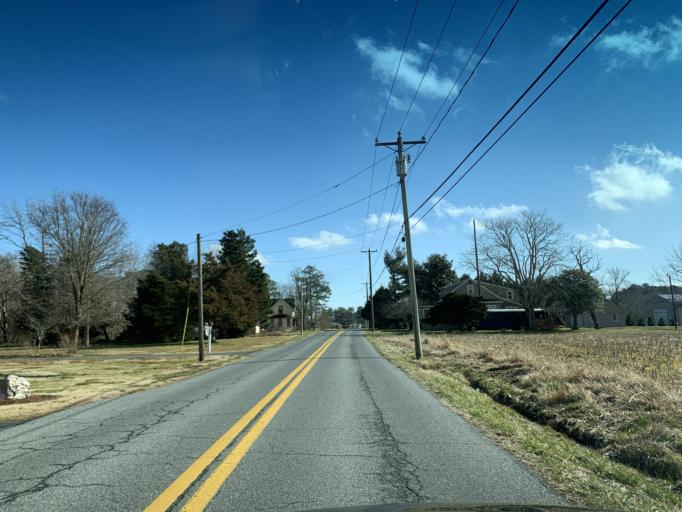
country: US
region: Delaware
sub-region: Sussex County
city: Selbyville
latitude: 38.4544
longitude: -75.2011
